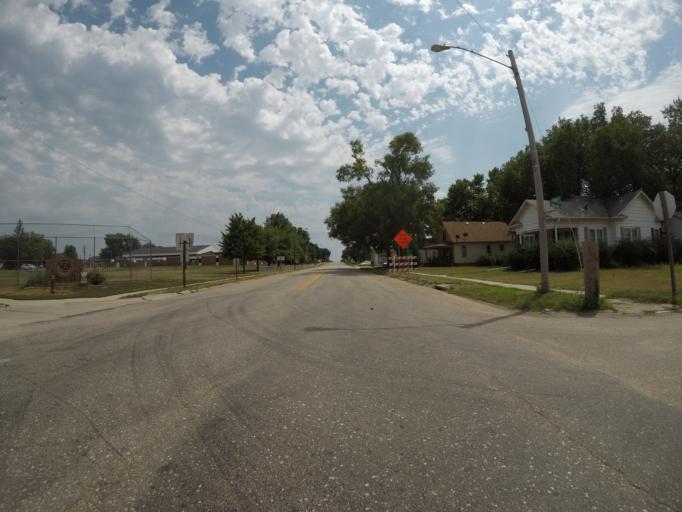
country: US
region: Nebraska
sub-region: Clay County
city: Clay Center
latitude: 40.5248
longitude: -98.0516
